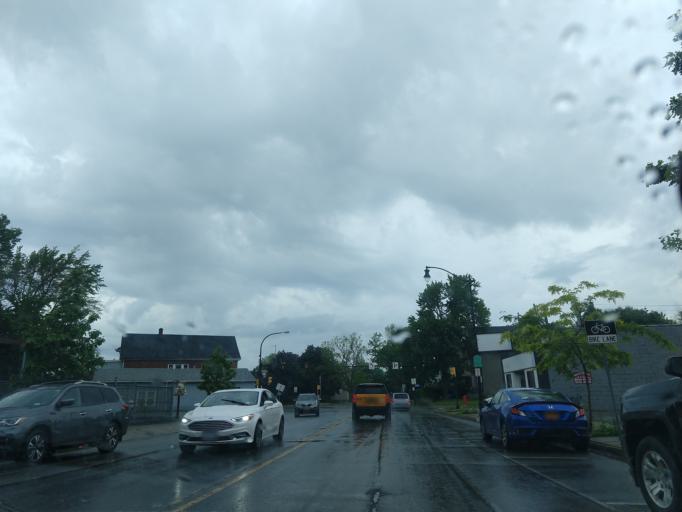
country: US
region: New York
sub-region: Erie County
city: Lackawanna
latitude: 42.8491
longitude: -78.8237
